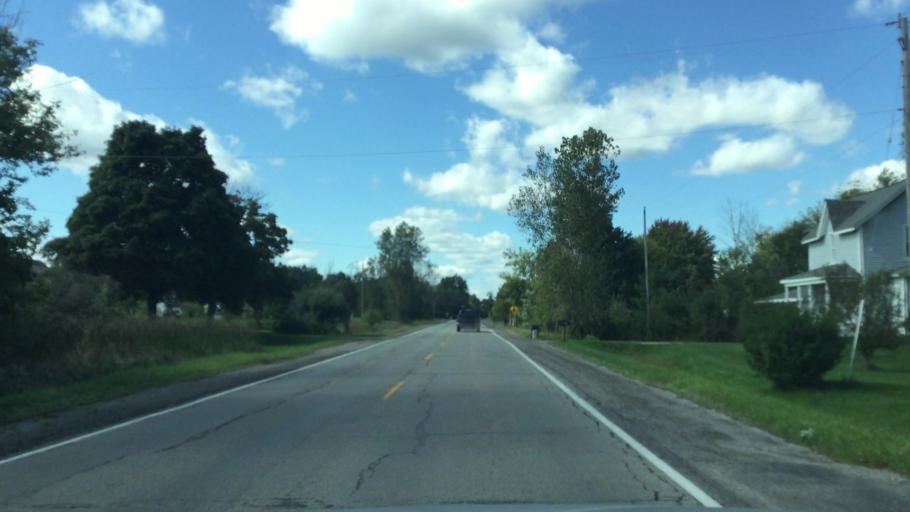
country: US
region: Michigan
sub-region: Genesee County
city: Swartz Creek
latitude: 42.9421
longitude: -83.8268
